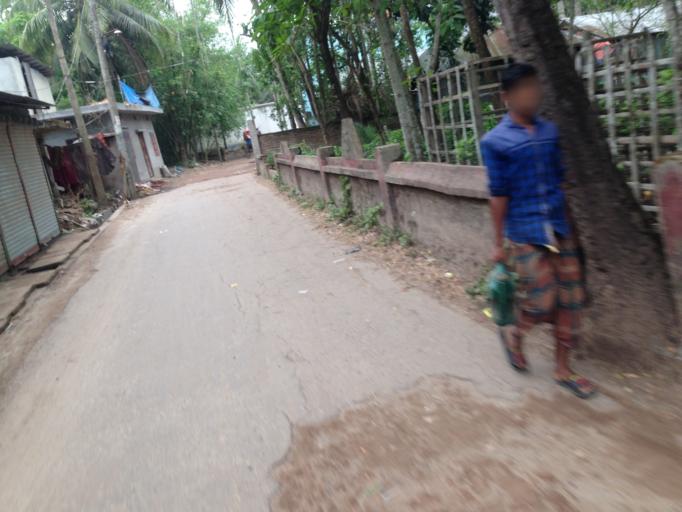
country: BD
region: Chittagong
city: Raipur
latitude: 23.0360
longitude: 90.7706
